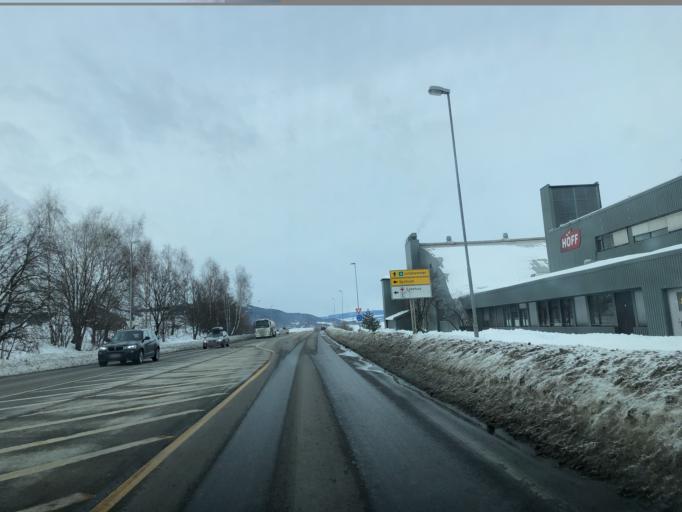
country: NO
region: Oppland
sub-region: Gjovik
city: Gjovik
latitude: 60.7962
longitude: 10.6964
